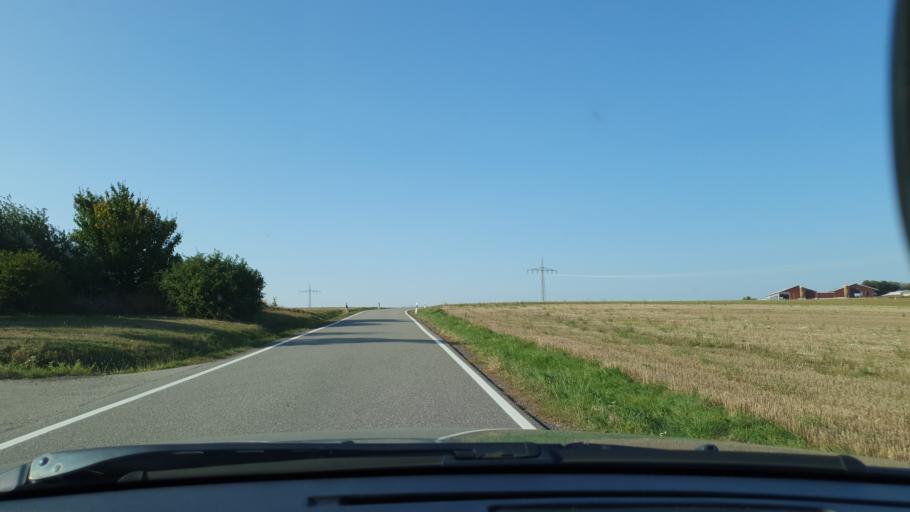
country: DE
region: Rheinland-Pfalz
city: Herschberg
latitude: 49.2859
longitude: 7.5577
